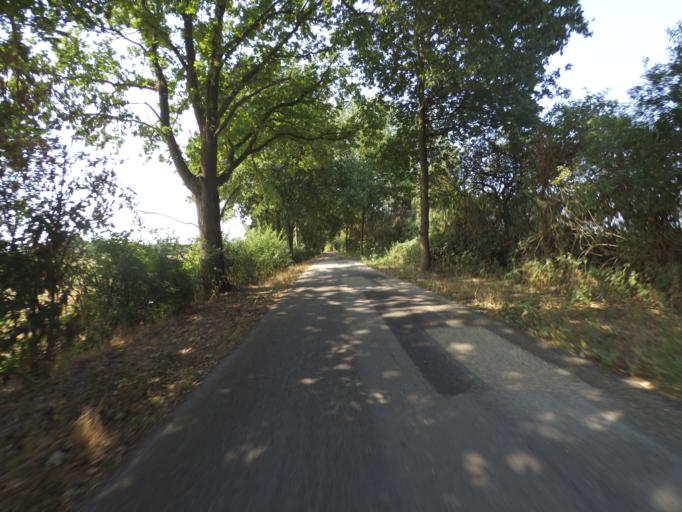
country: DE
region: North Rhine-Westphalia
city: Rees
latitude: 51.7873
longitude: 6.4140
